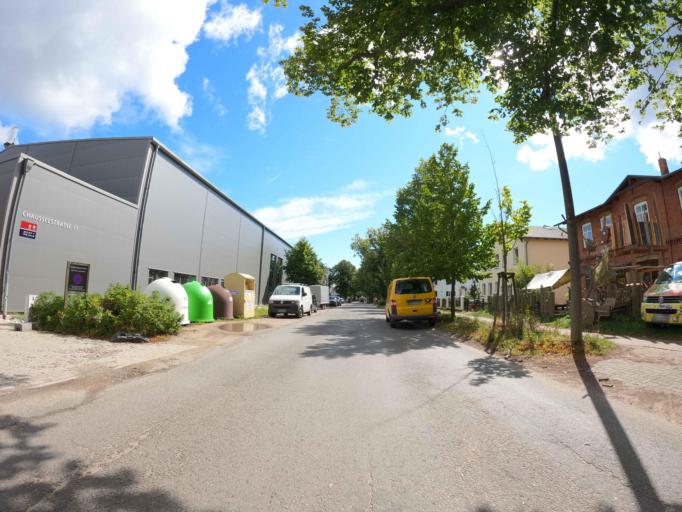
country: DE
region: Mecklenburg-Vorpommern
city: Putbus
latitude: 54.3450
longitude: 13.4997
